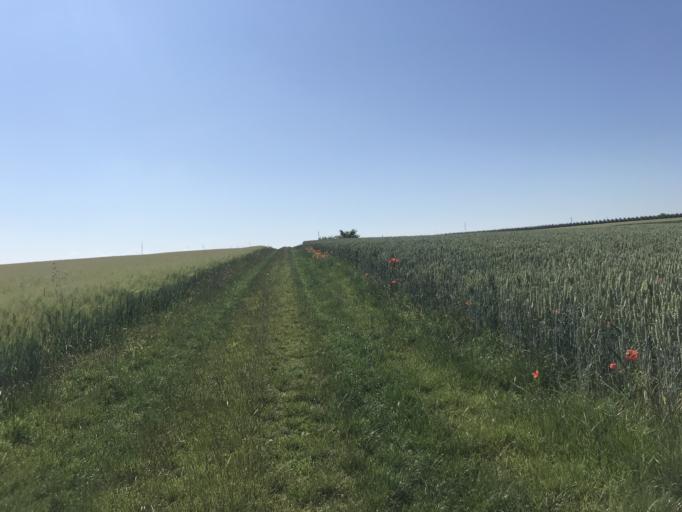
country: DE
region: Rheinland-Pfalz
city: Stadecken-Elsheim
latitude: 49.9391
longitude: 8.1258
